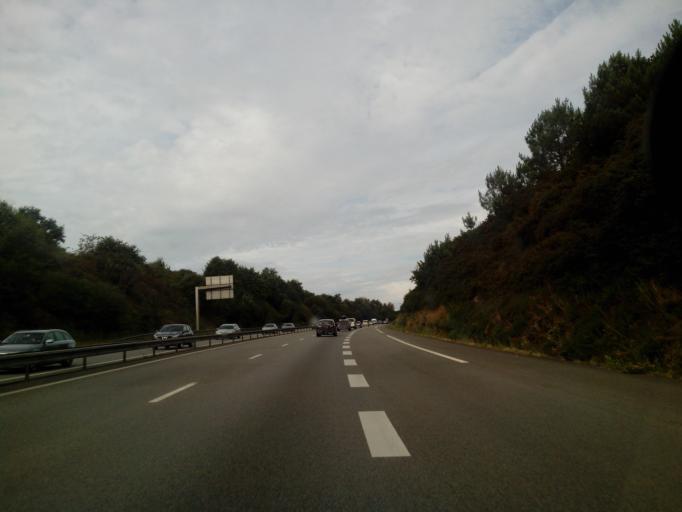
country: FR
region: Brittany
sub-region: Departement du Morbihan
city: Auray
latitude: 47.6567
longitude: -2.9910
